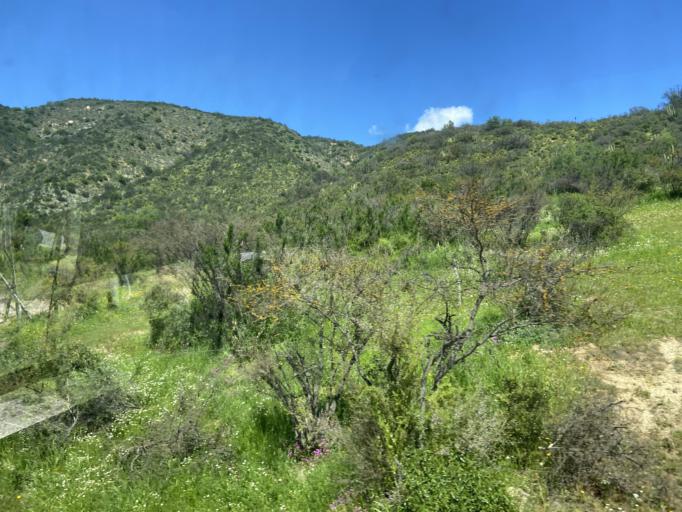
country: CL
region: Valparaiso
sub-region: Provincia de Marga Marga
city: Villa Alemana
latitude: -33.1923
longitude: -71.2838
